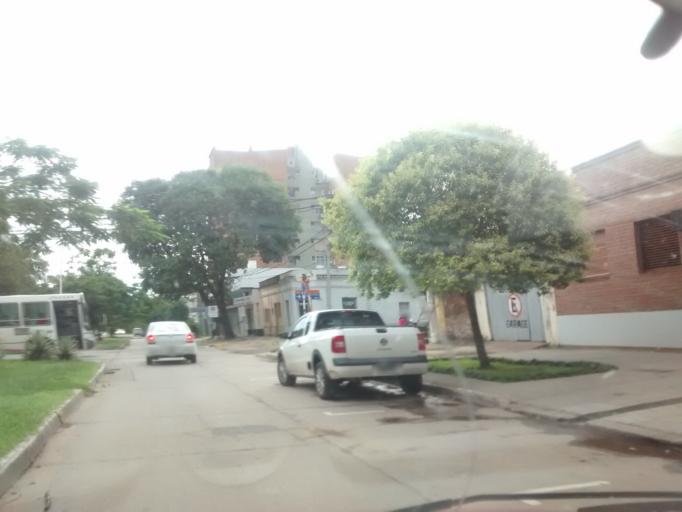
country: AR
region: Chaco
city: Resistencia
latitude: -27.4500
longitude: -58.9940
